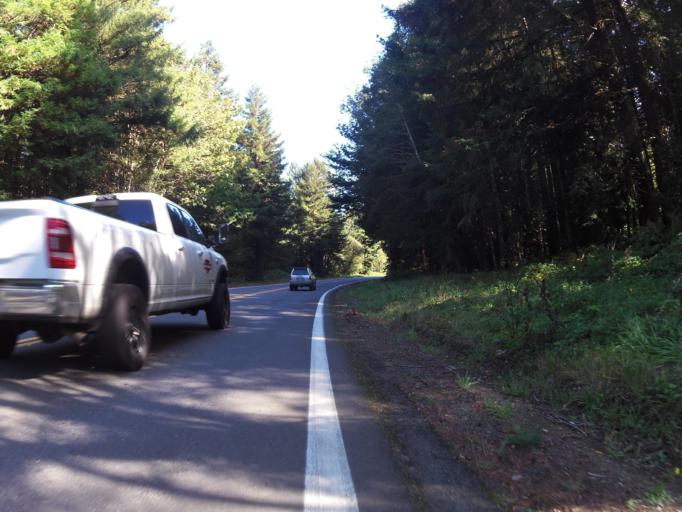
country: US
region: California
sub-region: Del Norte County
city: Bertsch-Oceanview
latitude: 41.8410
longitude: -124.1094
